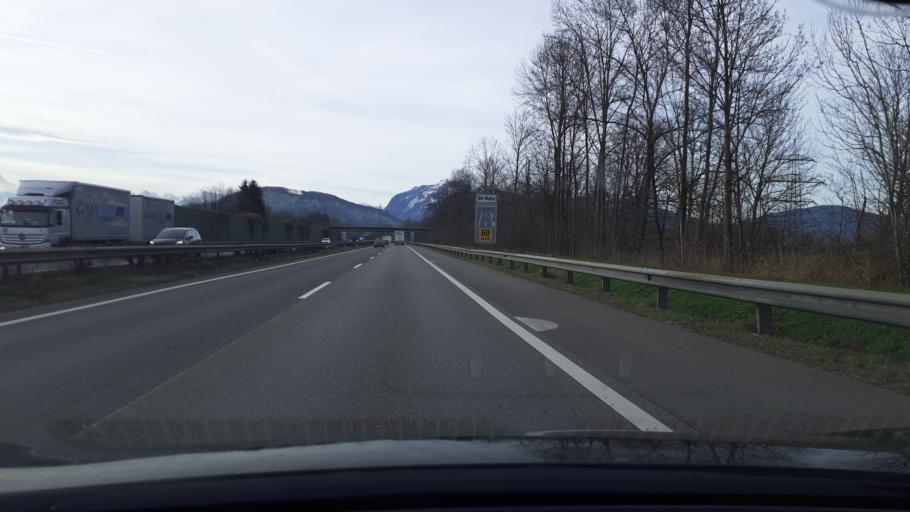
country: AT
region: Vorarlberg
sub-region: Politischer Bezirk Feldkirch
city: Altach
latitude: 47.3633
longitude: 9.6520
